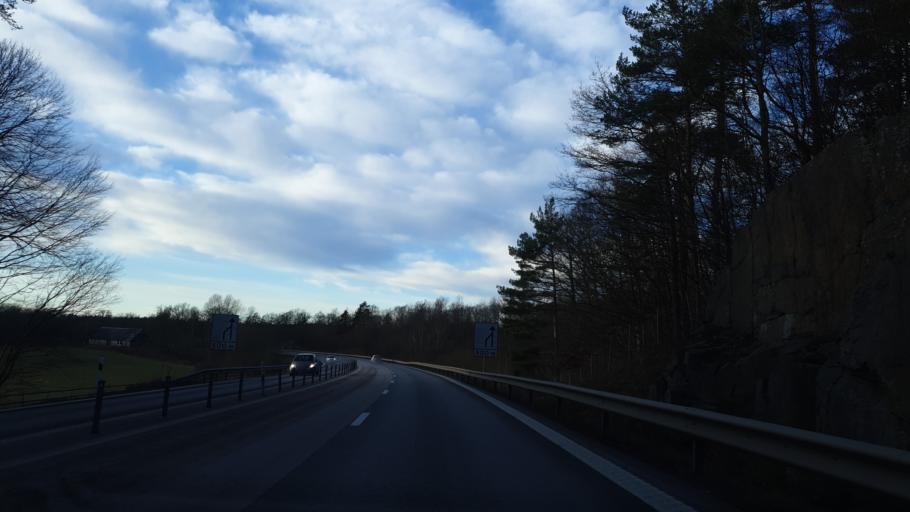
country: SE
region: Blekinge
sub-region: Karlshamns Kommun
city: Karlshamn
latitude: 56.1923
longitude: 14.8930
